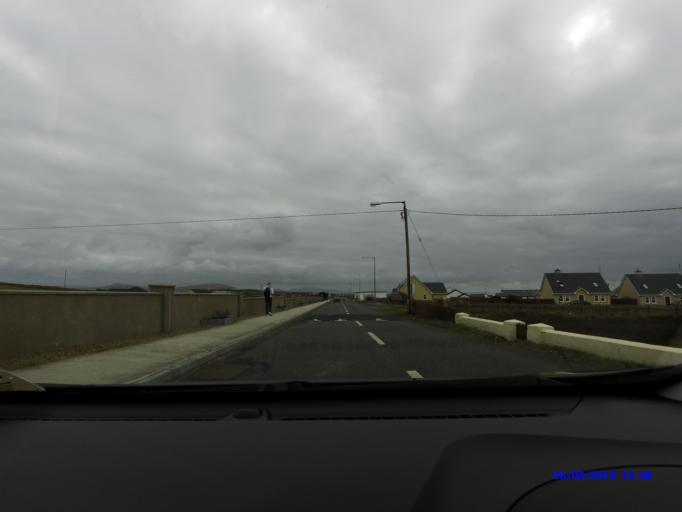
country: IE
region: Connaught
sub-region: Maigh Eo
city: Belmullet
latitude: 54.2172
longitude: -9.9813
